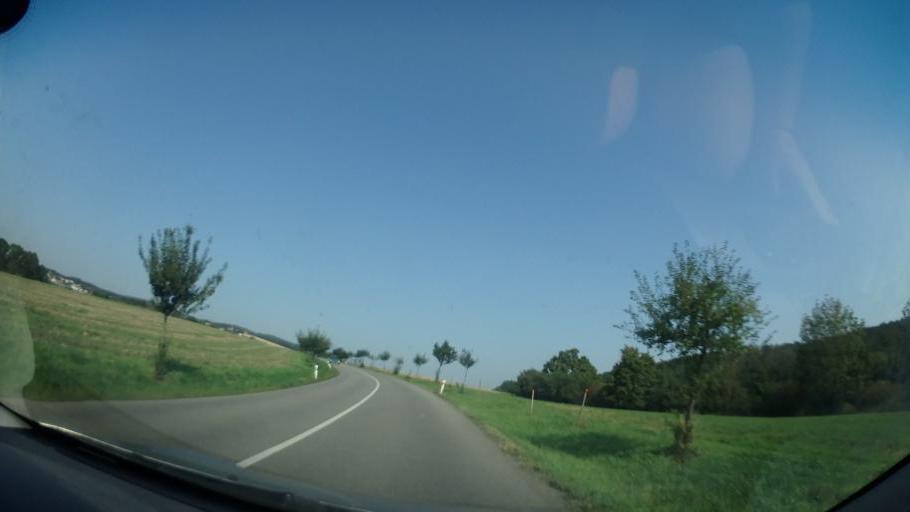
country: CZ
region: South Moravian
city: Kurim
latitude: 49.2460
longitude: 16.5296
